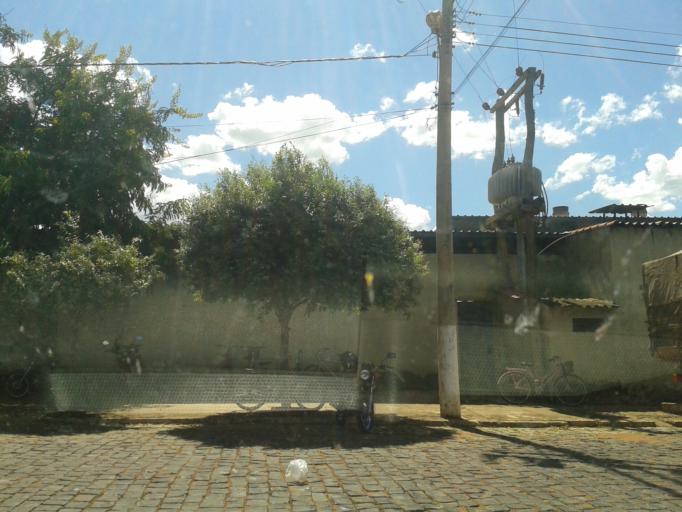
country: BR
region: Minas Gerais
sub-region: Santa Vitoria
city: Santa Vitoria
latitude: -18.6915
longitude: -49.9461
